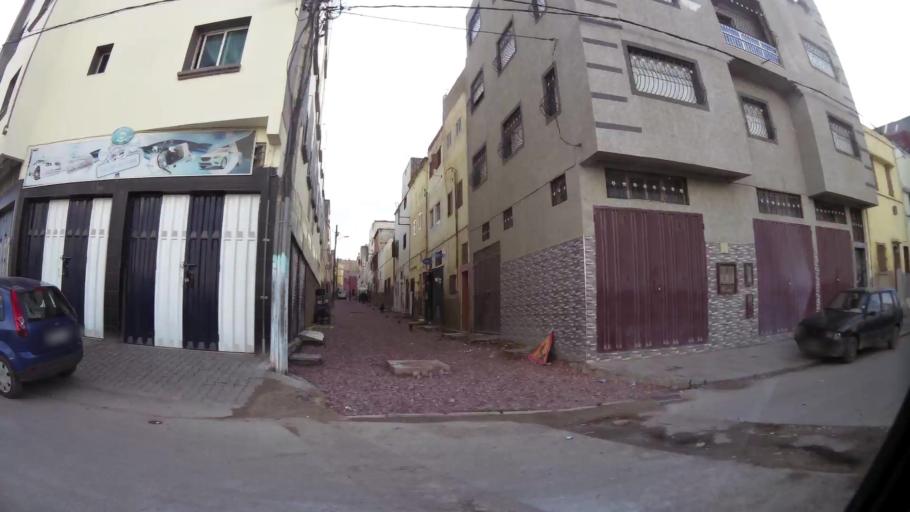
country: MA
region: Chaouia-Ouardigha
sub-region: Settat Province
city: Settat
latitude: 33.0095
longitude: -7.6230
